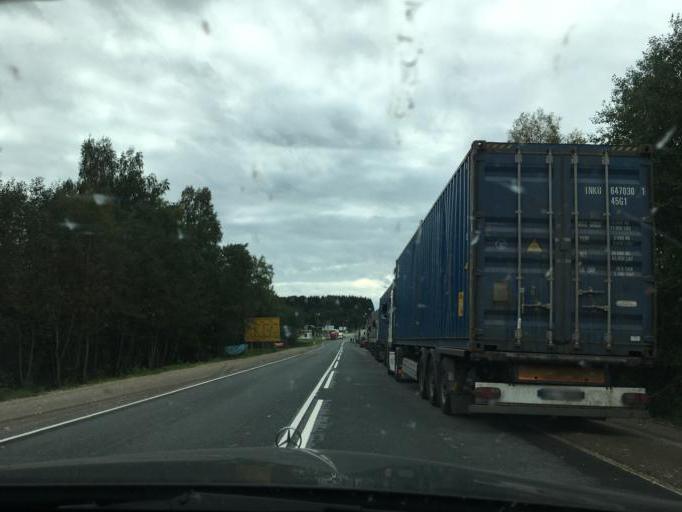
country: RU
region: Pskov
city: Pechory
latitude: 57.6471
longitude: 27.4030
